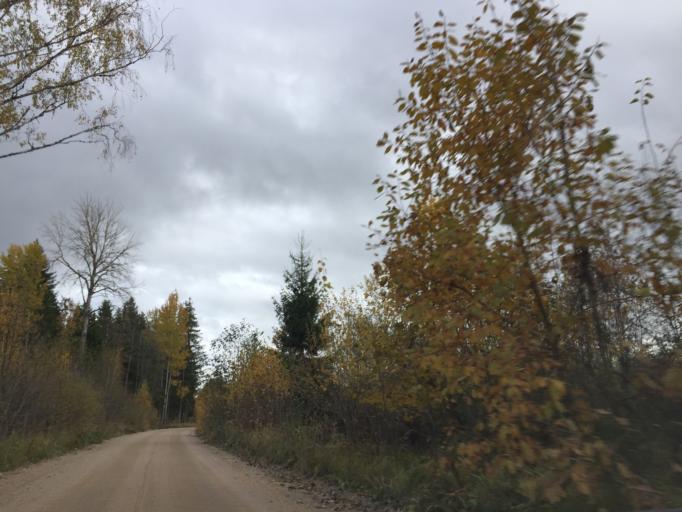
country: LV
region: Salacgrivas
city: Salacgriva
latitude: 57.5707
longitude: 24.3967
